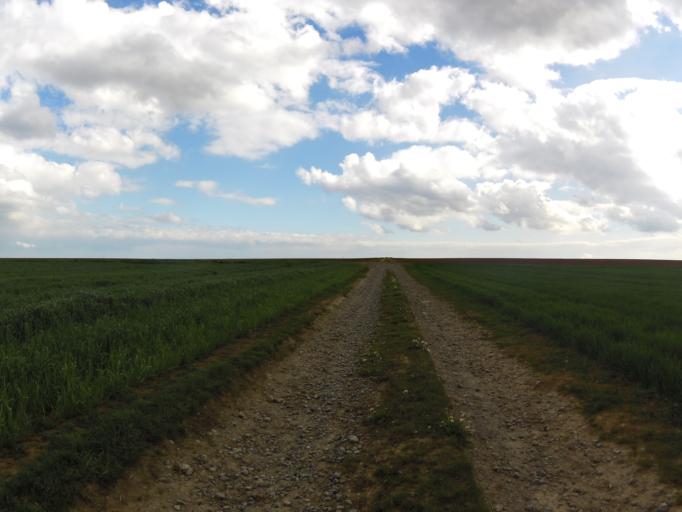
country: DE
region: Bavaria
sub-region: Regierungsbezirk Unterfranken
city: Oberpleichfeld
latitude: 49.8574
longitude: 10.0796
